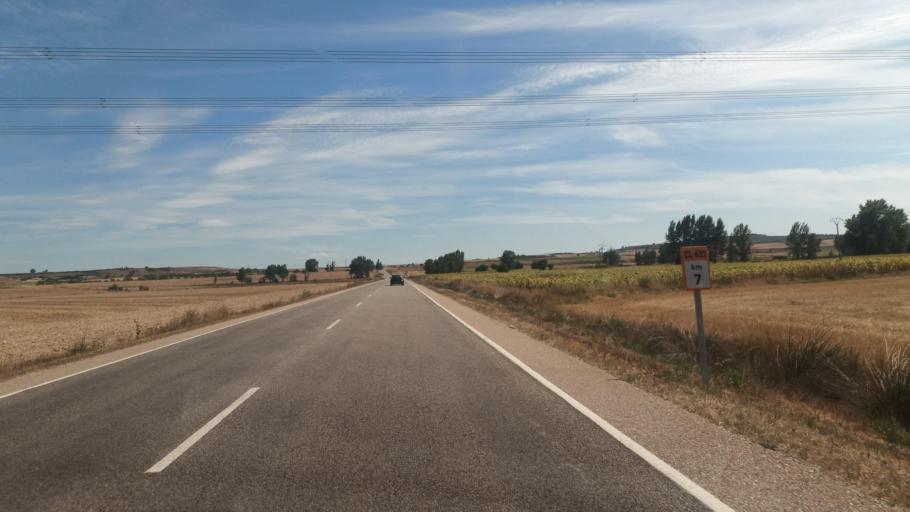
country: ES
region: Castille and Leon
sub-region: Provincia de Burgos
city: Aguilar de Bureba
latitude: 42.5920
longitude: -3.3429
